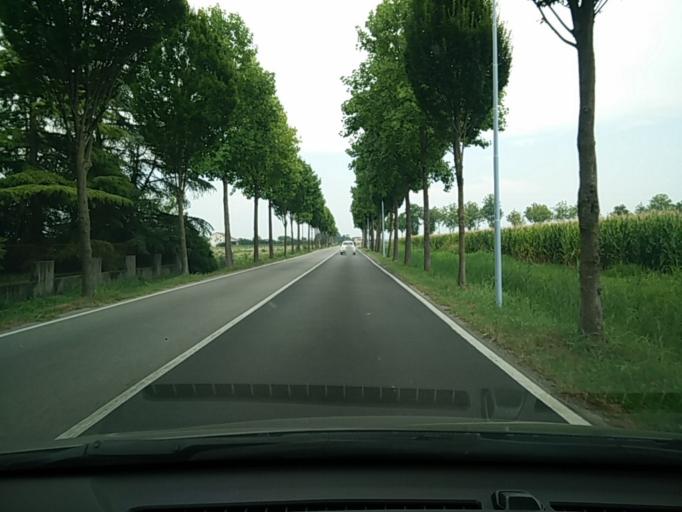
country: IT
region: Veneto
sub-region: Provincia di Venezia
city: Iesolo
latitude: 45.5348
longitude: 12.6501
